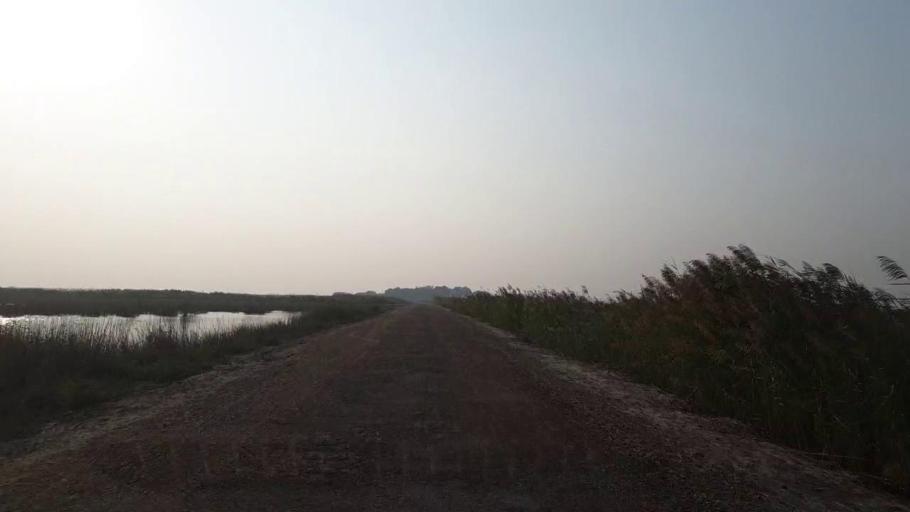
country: PK
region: Sindh
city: Bulri
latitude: 25.0850
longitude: 68.3124
